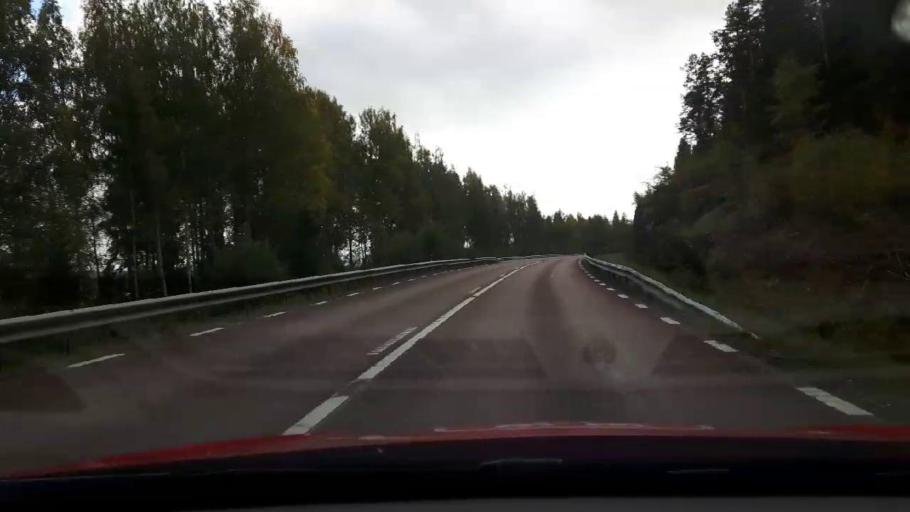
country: SE
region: Gaevleborg
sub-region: Bollnas Kommun
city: Arbra
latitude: 61.5565
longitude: 16.3463
